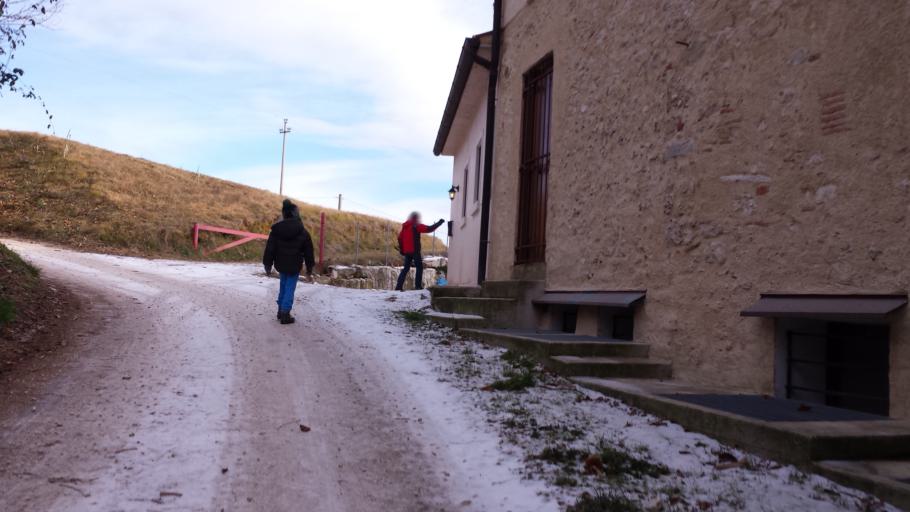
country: IT
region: Veneto
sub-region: Provincia di Treviso
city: Paderno del Grappa
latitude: 45.8437
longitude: 11.8574
